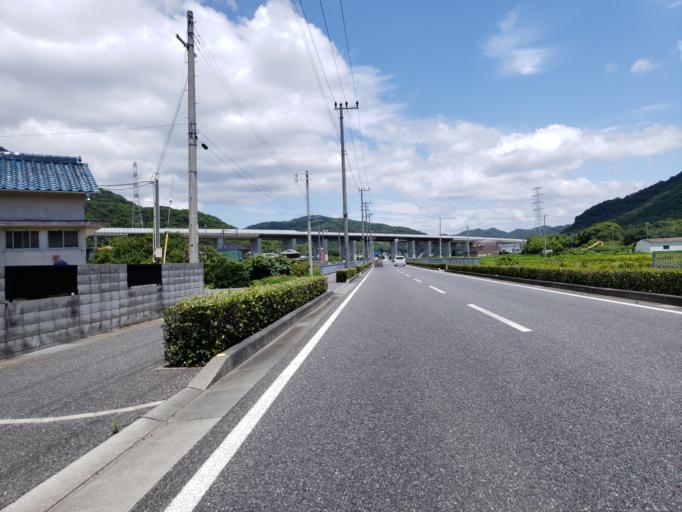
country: JP
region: Hyogo
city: Himeji
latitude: 34.8462
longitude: 134.7500
